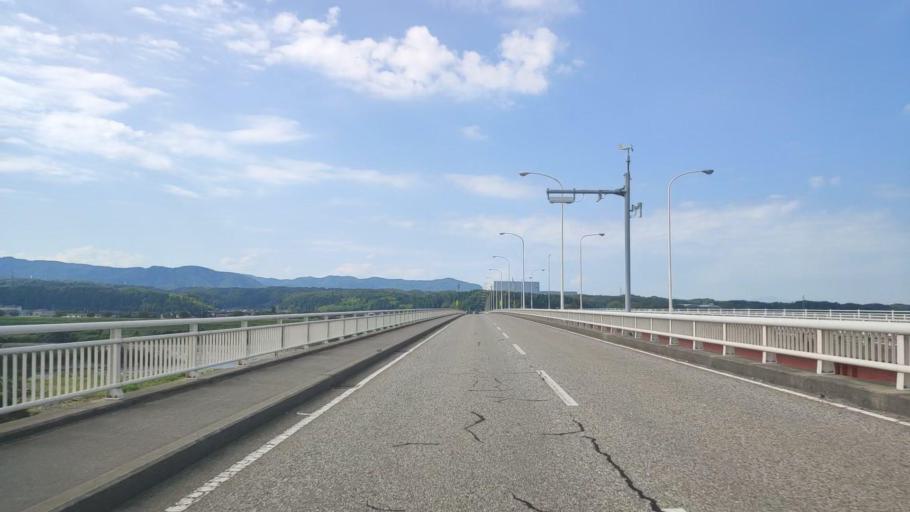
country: JP
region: Ishikawa
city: Matsuto
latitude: 36.4617
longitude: 136.5765
